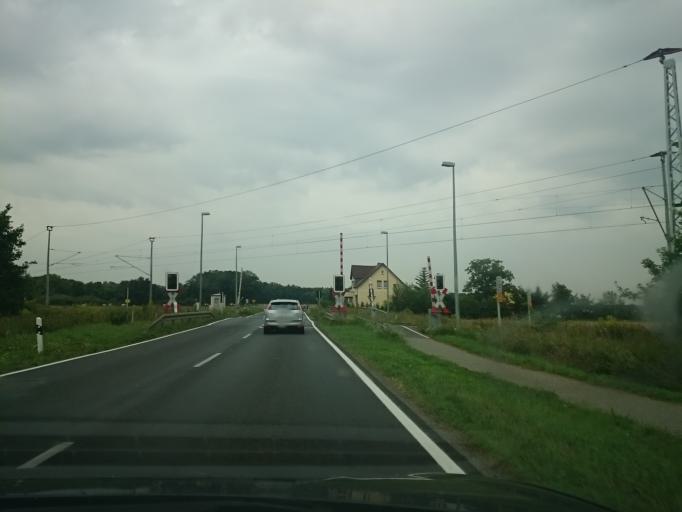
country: DE
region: Brandenburg
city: Gransee
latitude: 53.0298
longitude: 13.1875
